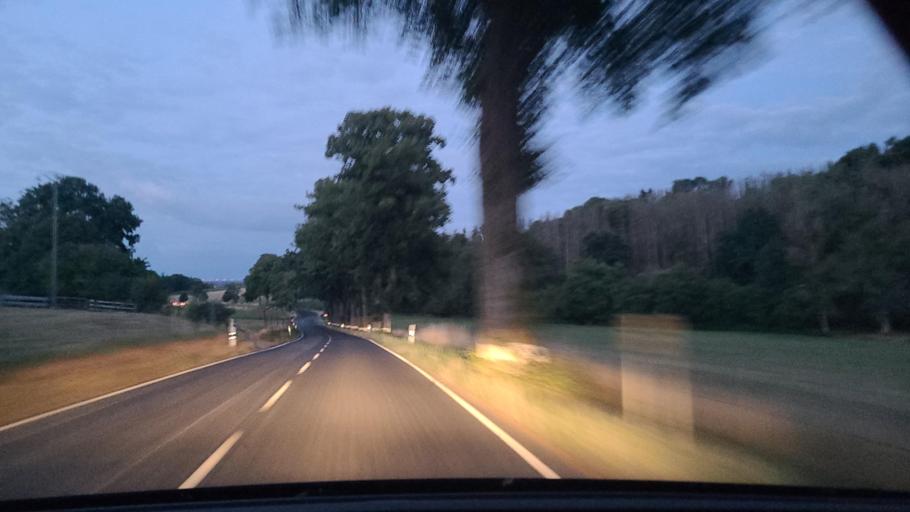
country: LU
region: Luxembourg
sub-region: Canton de Capellen
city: Garnich
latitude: 49.6080
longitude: 5.9382
